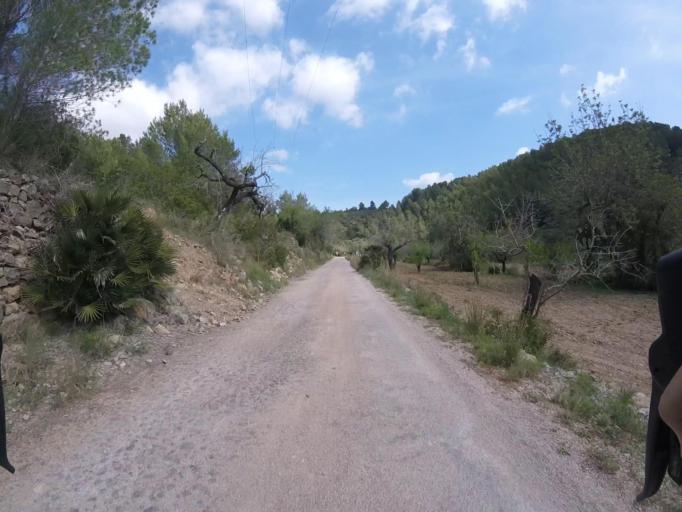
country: ES
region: Valencia
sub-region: Provincia de Castello
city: Cabanes
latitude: 40.1154
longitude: 0.0476
